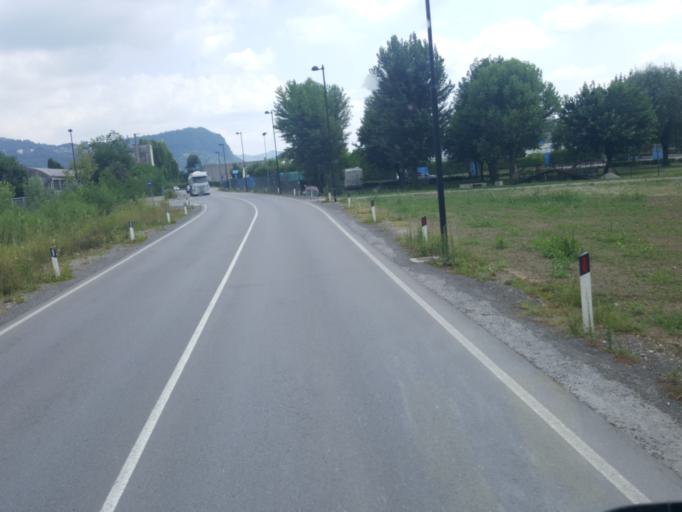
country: IT
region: Lombardy
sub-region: Provincia di Lecco
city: Calolziocorte
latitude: 45.7959
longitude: 9.4296
